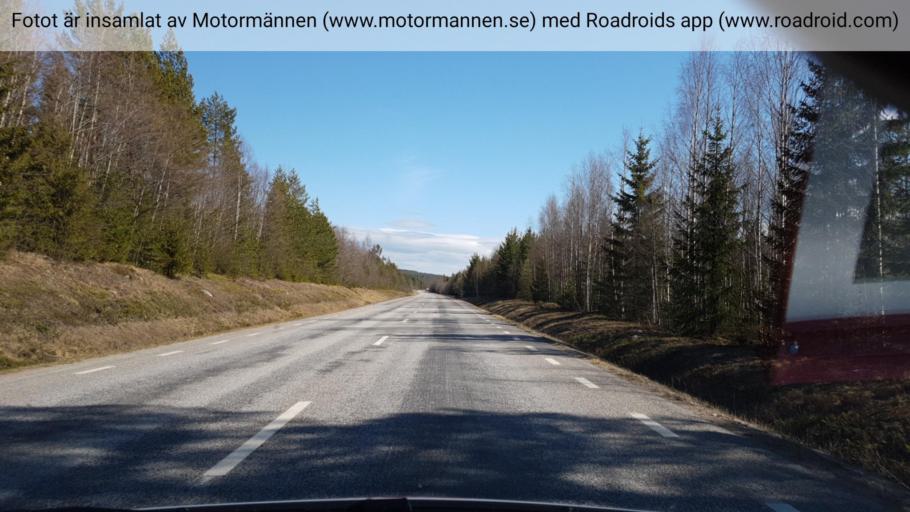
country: SE
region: Vaesternorrland
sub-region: Solleftea Kommun
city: As
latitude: 63.5086
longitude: 16.8493
